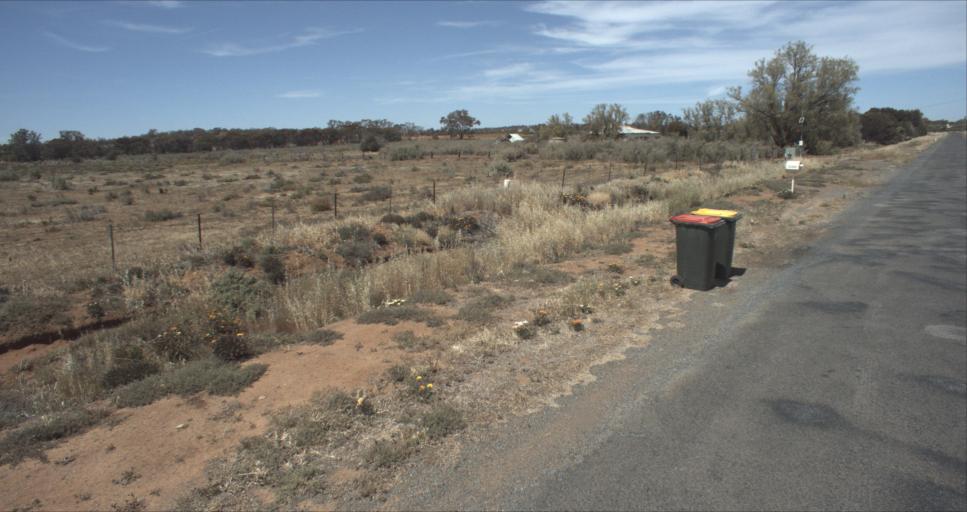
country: AU
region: New South Wales
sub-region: Leeton
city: Leeton
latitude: -34.6035
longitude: 146.4265
